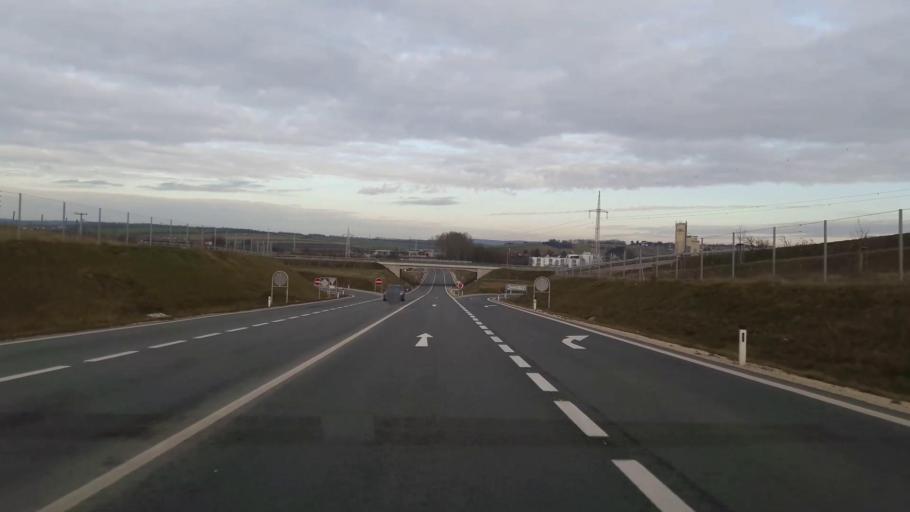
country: AT
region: Lower Austria
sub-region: Politischer Bezirk Mistelbach
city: Mistelbach
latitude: 48.5524
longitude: 16.5596
